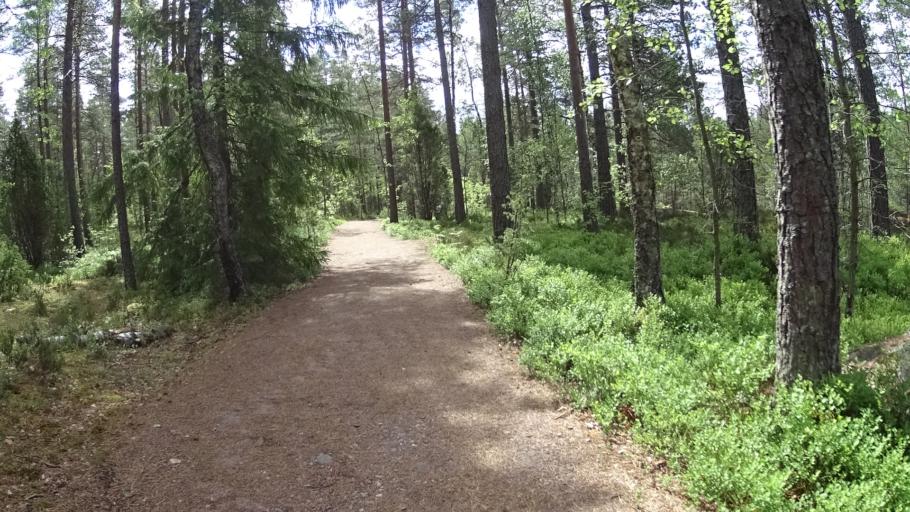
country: FI
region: Uusimaa
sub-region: Helsinki
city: Espoo
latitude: 60.2947
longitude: 24.5194
